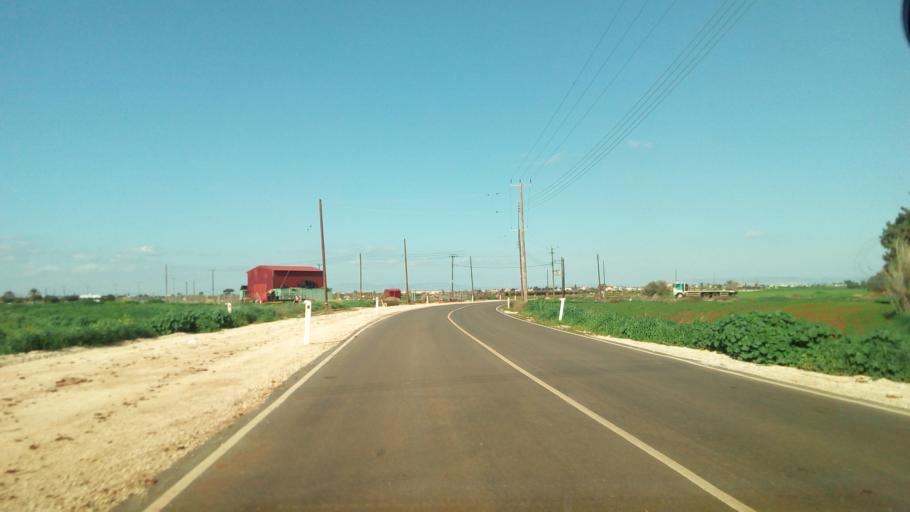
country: CY
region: Ammochostos
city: Avgorou
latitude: 35.0116
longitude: 33.8439
